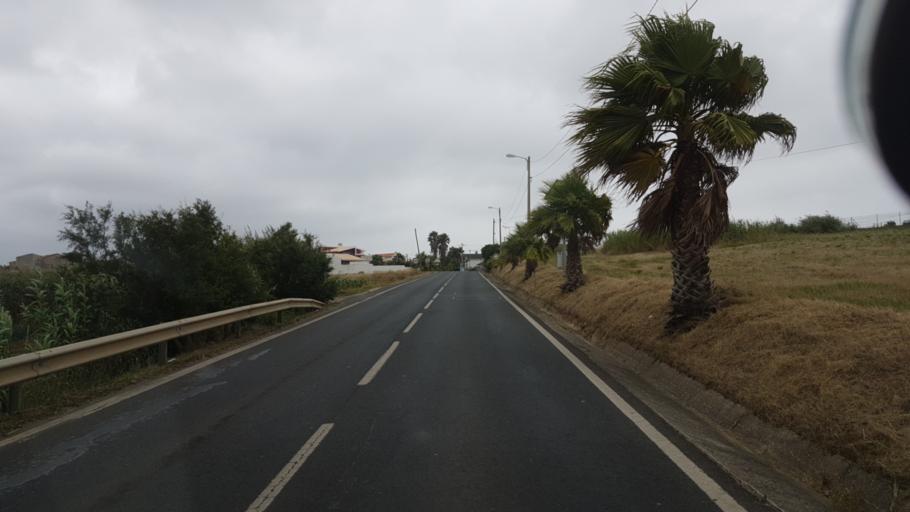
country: PT
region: Lisbon
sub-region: Lourinha
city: Lourinha
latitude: 39.2170
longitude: -9.3212
